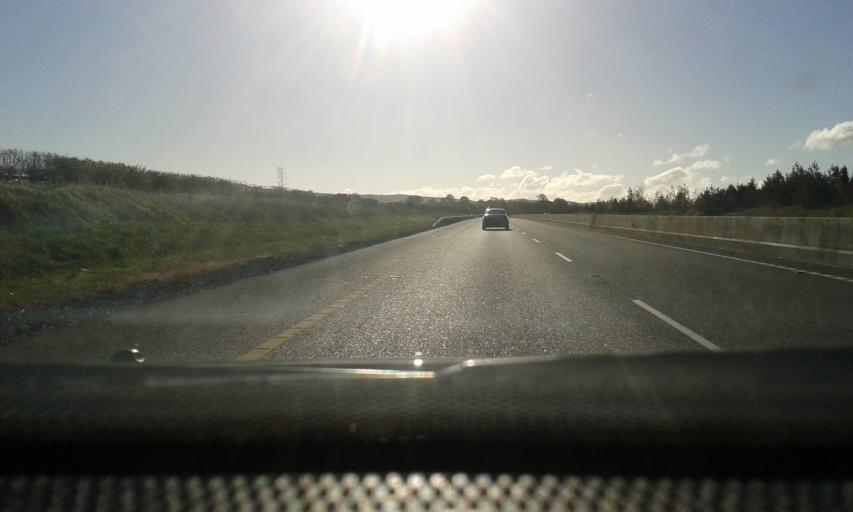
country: IE
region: Leinster
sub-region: Laois
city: Rathdowney
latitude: 52.8356
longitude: -7.5013
